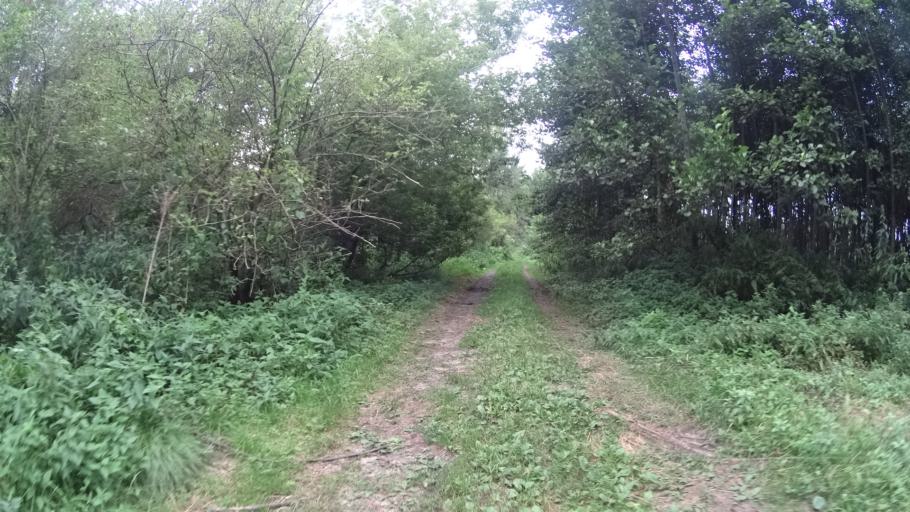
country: PL
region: Masovian Voivodeship
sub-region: Powiat grojecki
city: Mogielnica
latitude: 51.6679
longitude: 20.7445
